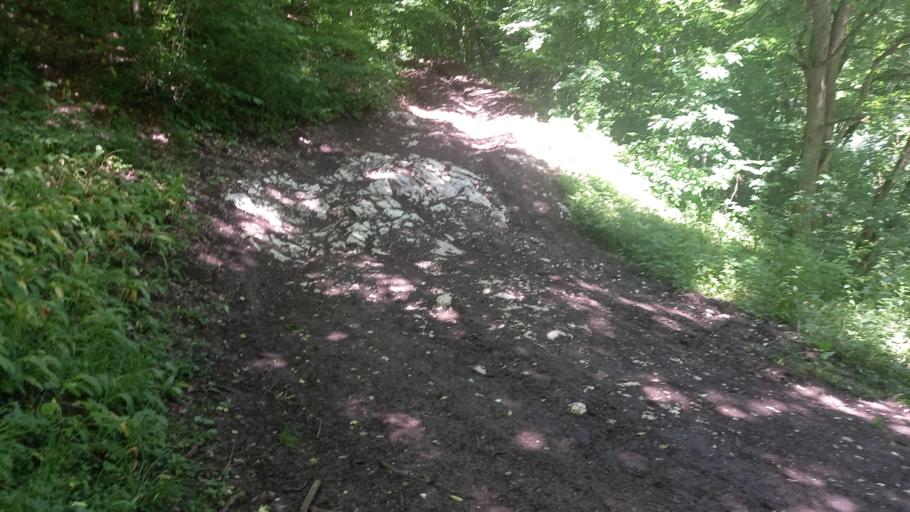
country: RU
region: Karachayevo-Cherkesiya
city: Pregradnaya
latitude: 44.1035
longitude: 41.1381
